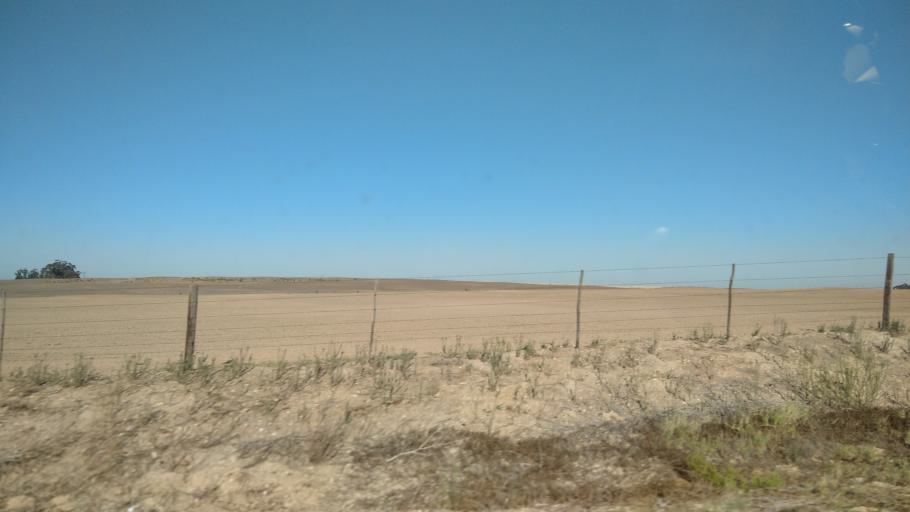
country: ZA
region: Western Cape
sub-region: West Coast District Municipality
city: Moorreesburg
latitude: -33.1415
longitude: 18.4585
